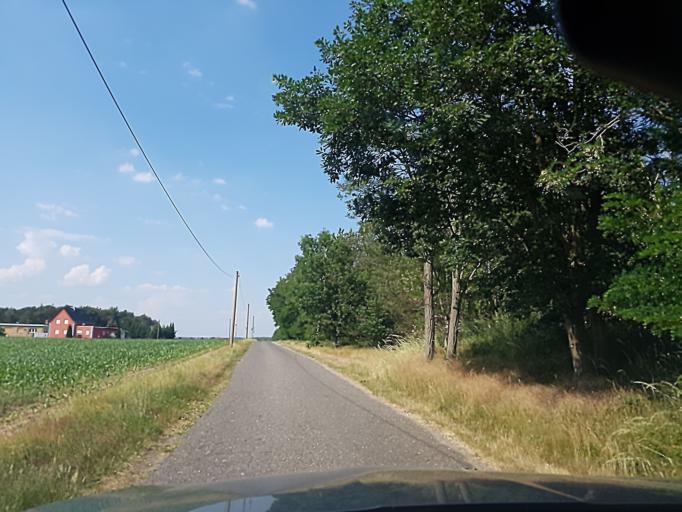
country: DE
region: Brandenburg
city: Ruckersdorf
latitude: 51.5598
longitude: 13.5588
